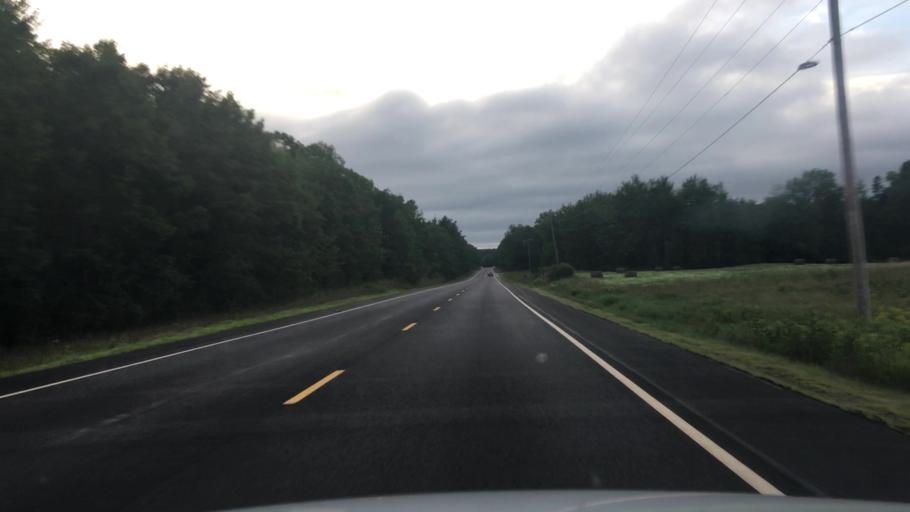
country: US
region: Maine
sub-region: Waldo County
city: Searsmont
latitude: 44.4033
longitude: -69.1659
